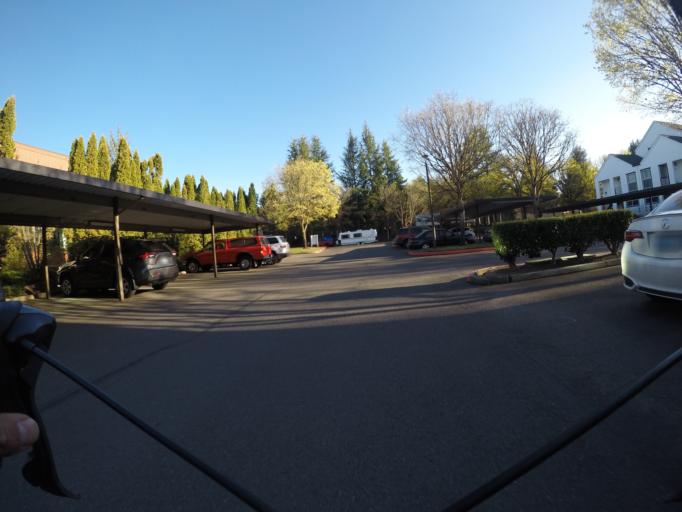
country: US
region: Oregon
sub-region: Washington County
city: Oak Hills
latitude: 45.5203
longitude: -122.8421
